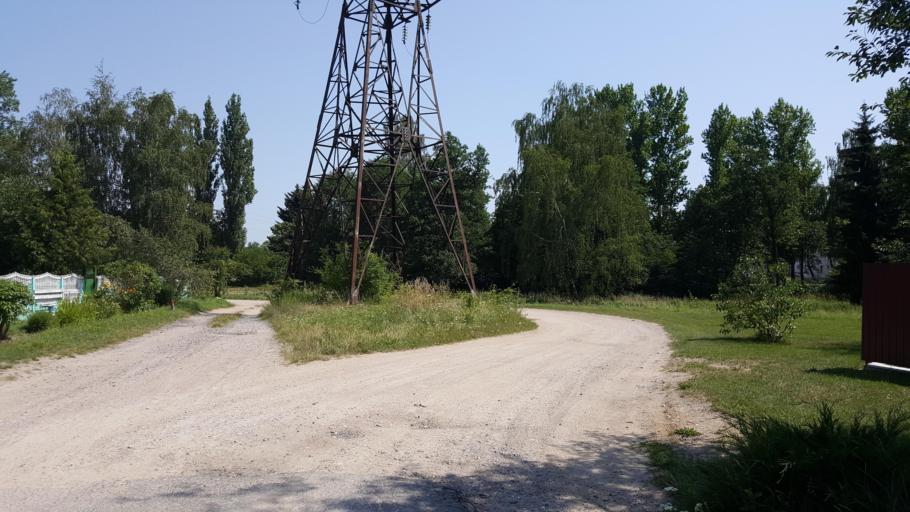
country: BY
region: Brest
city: Zhabinka
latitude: 52.1913
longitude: 24.0154
